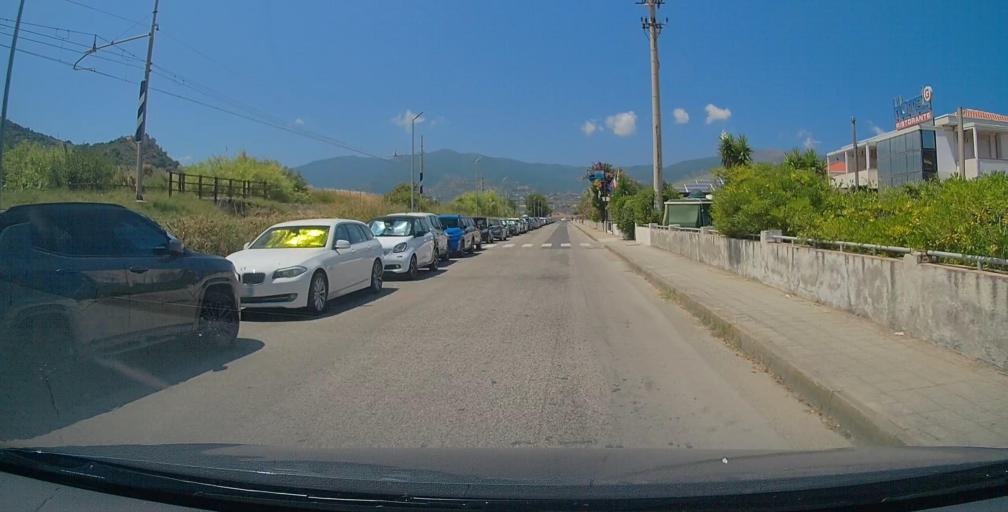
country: IT
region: Sicily
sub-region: Messina
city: Oliveri
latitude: 38.1477
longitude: 15.0182
